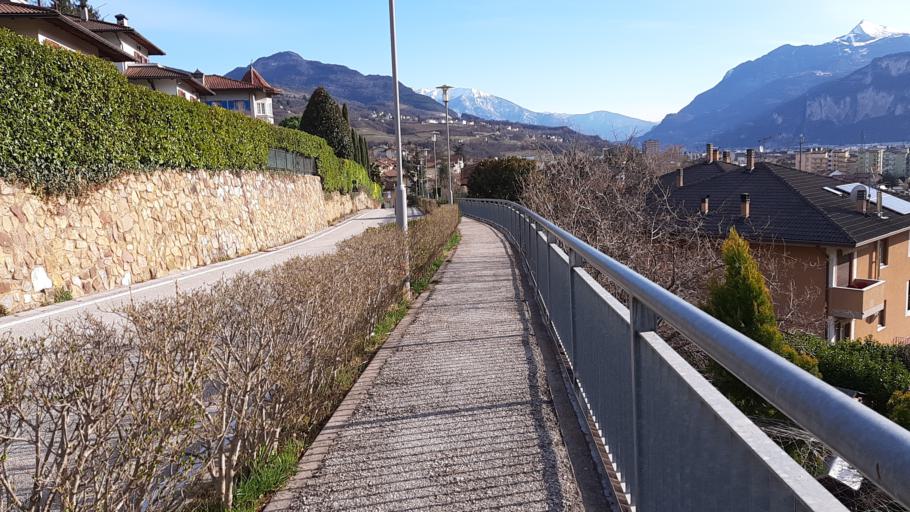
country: IT
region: Trentino-Alto Adige
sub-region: Provincia di Trento
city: Lavis
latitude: 46.1467
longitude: 11.1110
